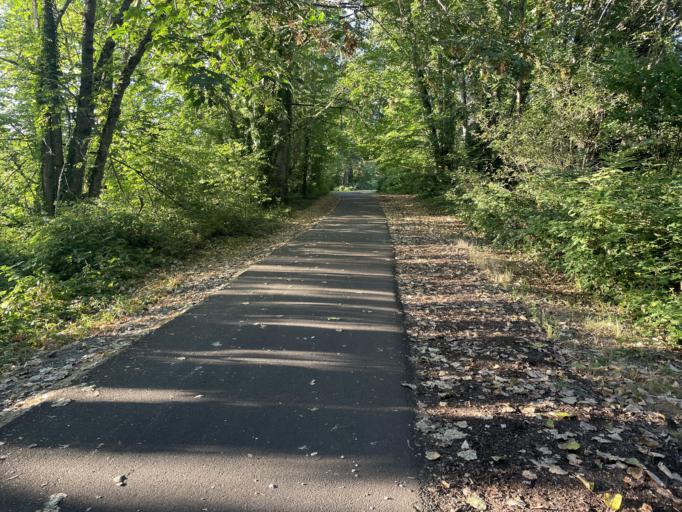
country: US
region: Oregon
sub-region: Marion County
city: Salem
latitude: 44.9225
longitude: -123.0748
